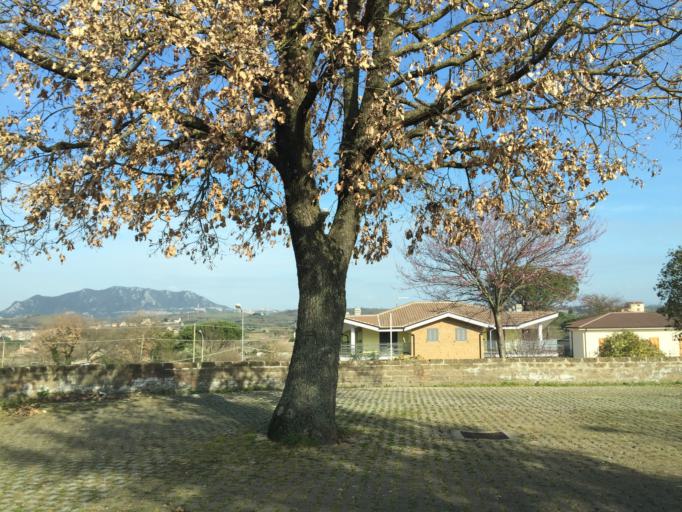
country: IT
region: Latium
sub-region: Provincia di Viterbo
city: Calcata Nuova
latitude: 42.2168
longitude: 12.4259
